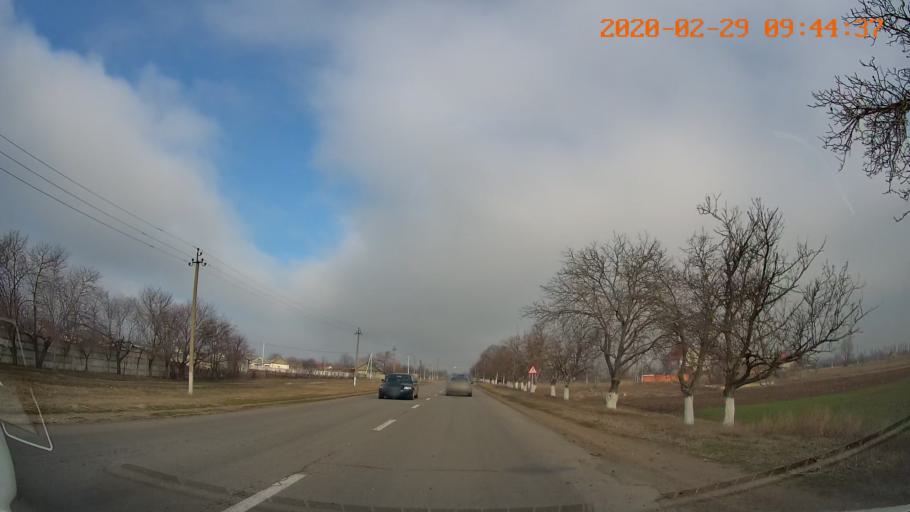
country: MD
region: Telenesti
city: Crasnoe
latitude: 46.6542
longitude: 29.8153
